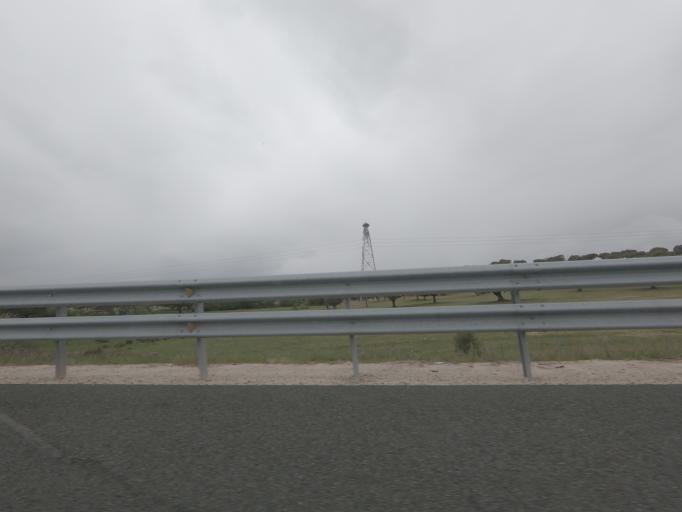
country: ES
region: Extremadura
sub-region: Provincia de Caceres
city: Jarilla
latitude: 40.1827
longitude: -6.0150
